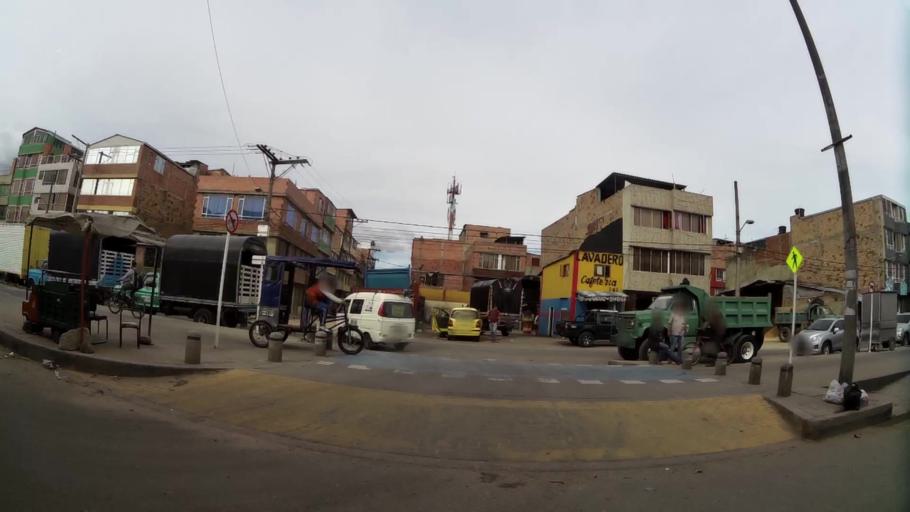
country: CO
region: Cundinamarca
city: Soacha
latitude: 4.6329
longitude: -74.1663
